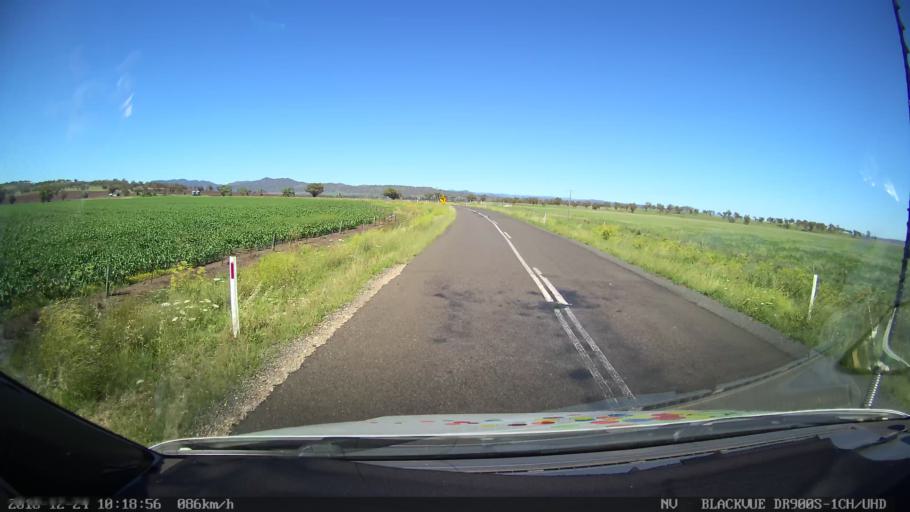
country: AU
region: New South Wales
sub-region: Liverpool Plains
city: Quirindi
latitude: -31.7258
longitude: 150.5691
